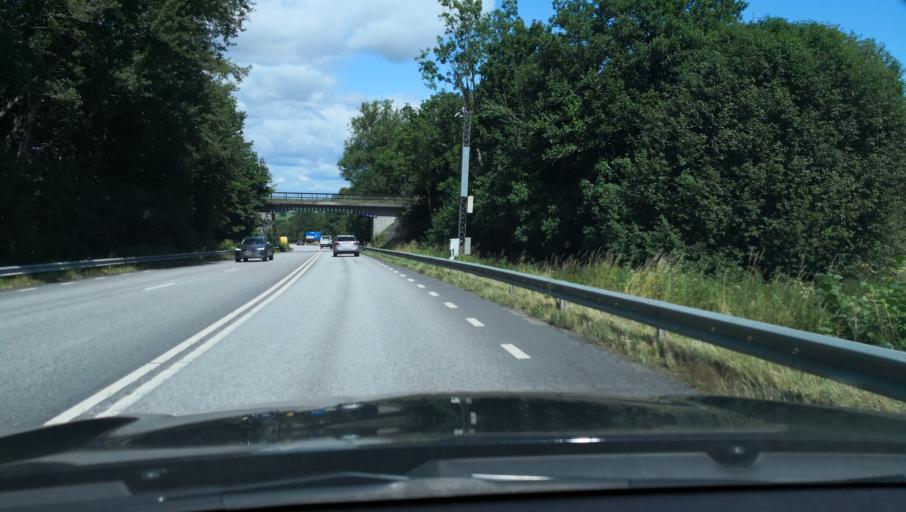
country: SE
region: Skane
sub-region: Kristianstads Kommun
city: Degeberga
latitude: 55.8000
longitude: 14.1487
